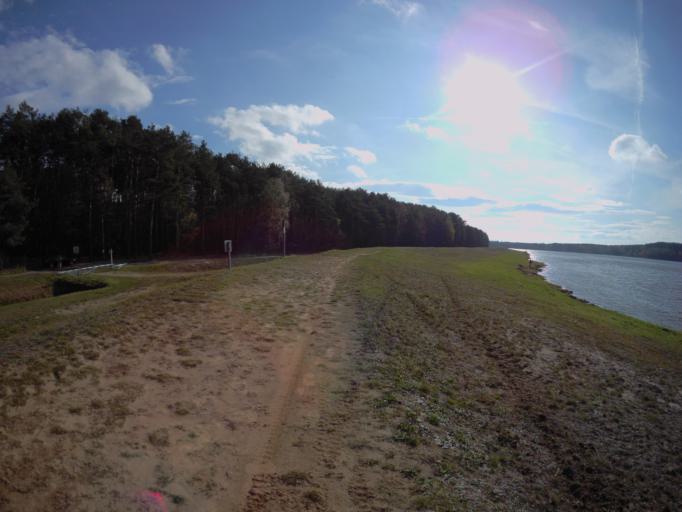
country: PL
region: Subcarpathian Voivodeship
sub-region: Powiat kolbuszowski
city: Lipnica
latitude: 50.3350
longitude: 21.9439
